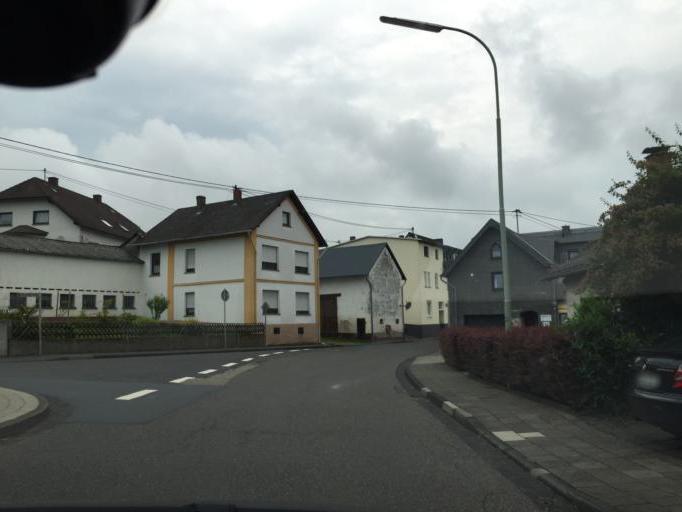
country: DE
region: Rheinland-Pfalz
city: Bonefeld
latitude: 50.5245
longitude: 7.4896
